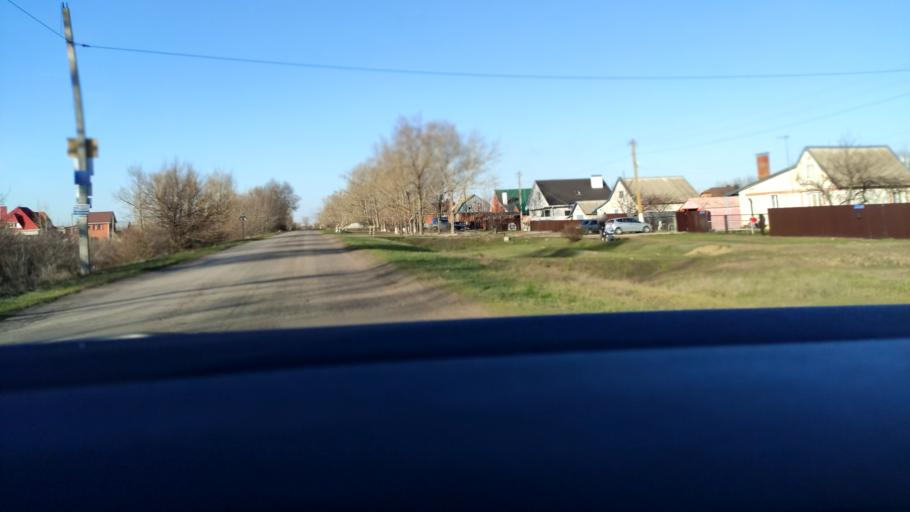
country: RU
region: Voronezj
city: Maslovka
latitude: 51.5115
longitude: 39.2957
